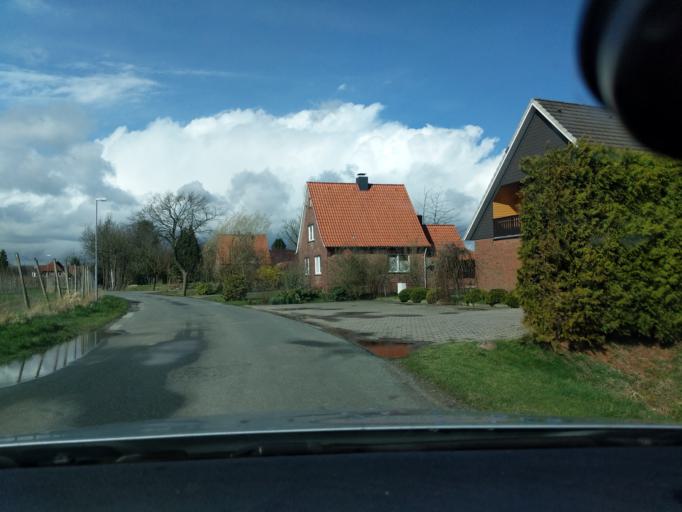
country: DE
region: Lower Saxony
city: Stade
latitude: 53.6100
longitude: 9.5118
